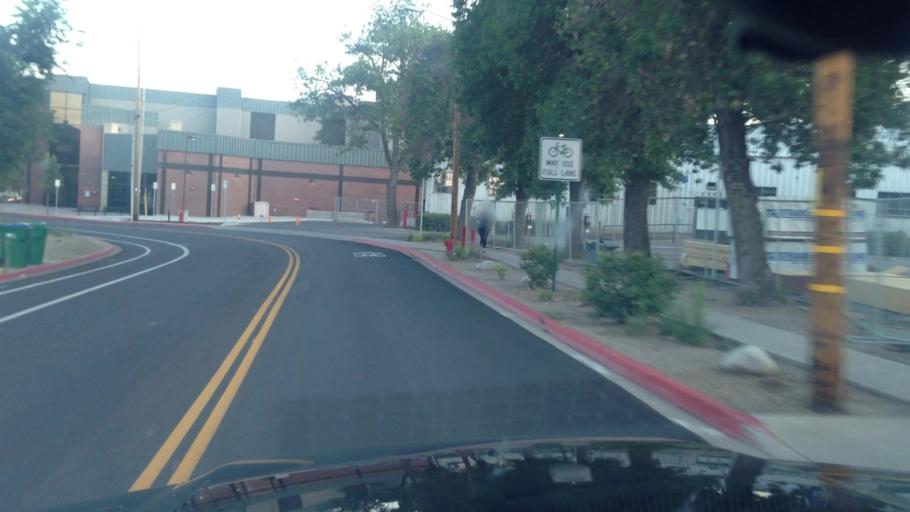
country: US
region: Nevada
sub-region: Washoe County
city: Reno
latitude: 39.5415
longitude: -119.8127
